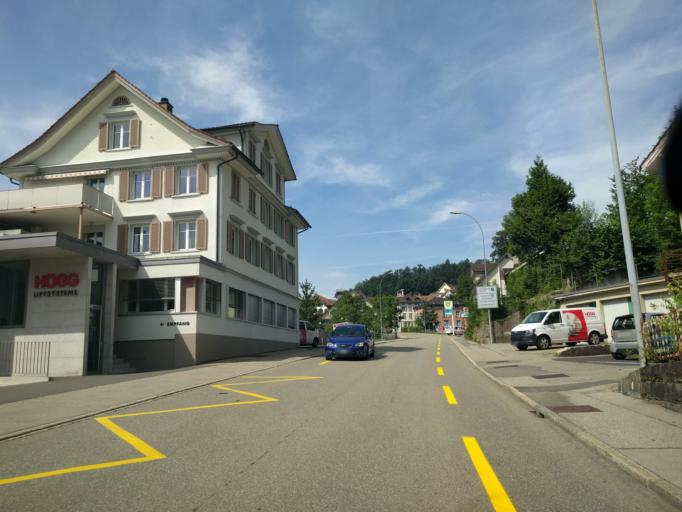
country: CH
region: Saint Gallen
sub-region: Wahlkreis Toggenburg
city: Lichtensteig
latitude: 47.3202
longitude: 9.0875
